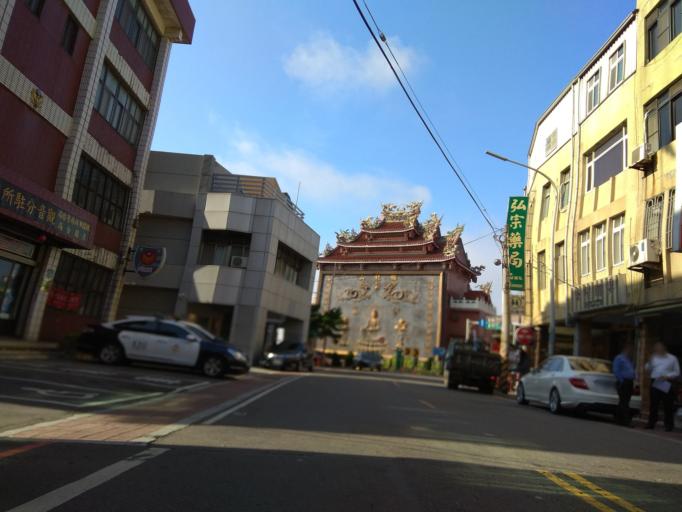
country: TW
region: Taiwan
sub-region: Hsinchu
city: Zhubei
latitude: 25.0365
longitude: 121.0823
